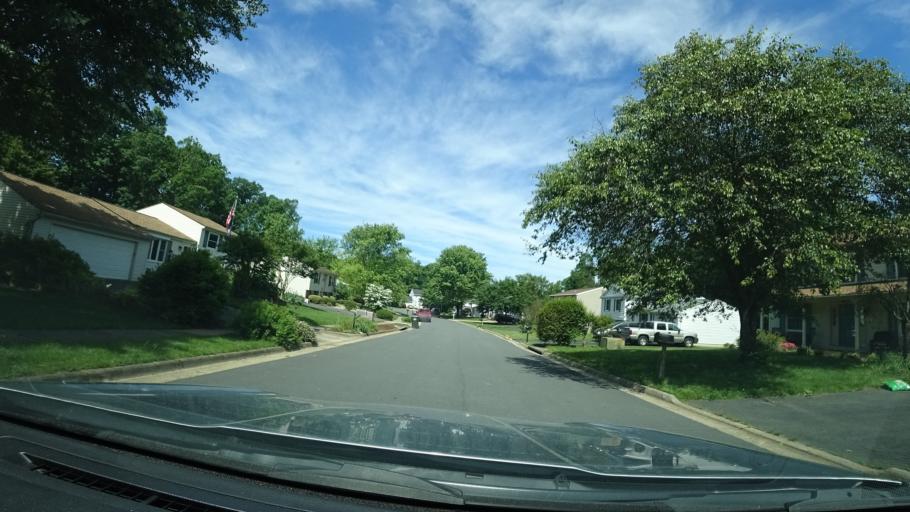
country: US
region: Virginia
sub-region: Loudoun County
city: Oak Grove
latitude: 38.9884
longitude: -77.4053
